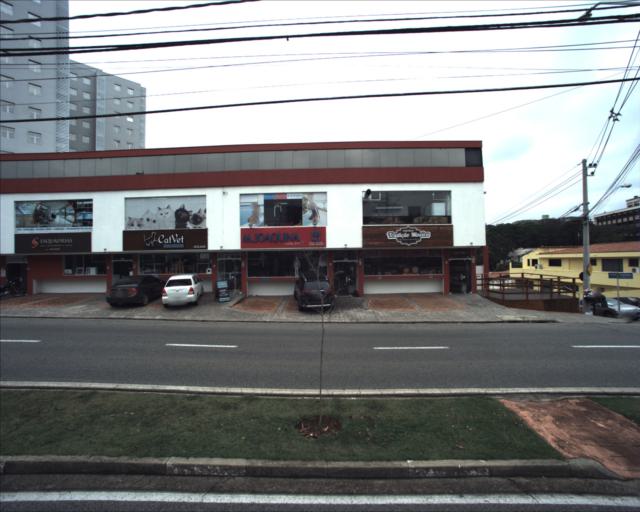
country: BR
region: Sao Paulo
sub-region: Sorocaba
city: Sorocaba
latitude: -23.5124
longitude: -47.4583
